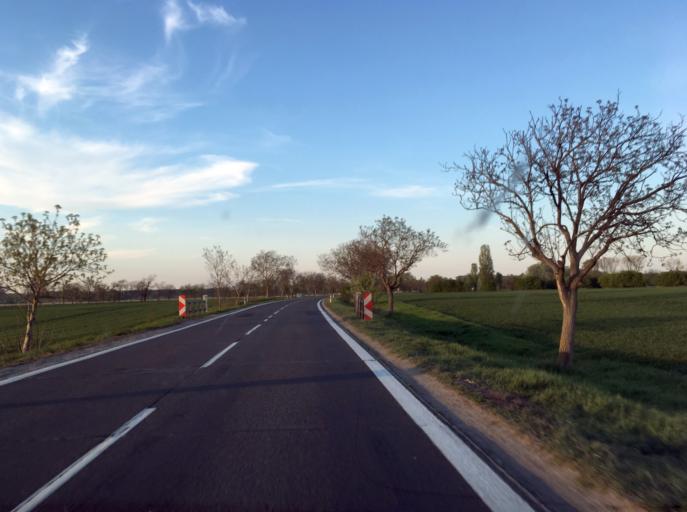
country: SK
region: Trnavsky
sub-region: Okres Dunajska Streda
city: Velky Meder
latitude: 47.8342
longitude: 17.7105
